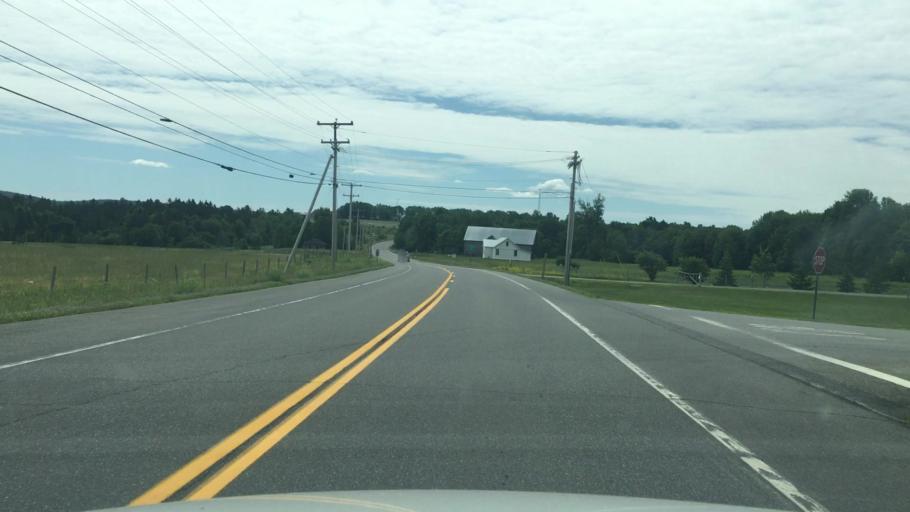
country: US
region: Maine
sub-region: Waldo County
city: Troy
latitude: 44.5510
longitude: -69.2681
